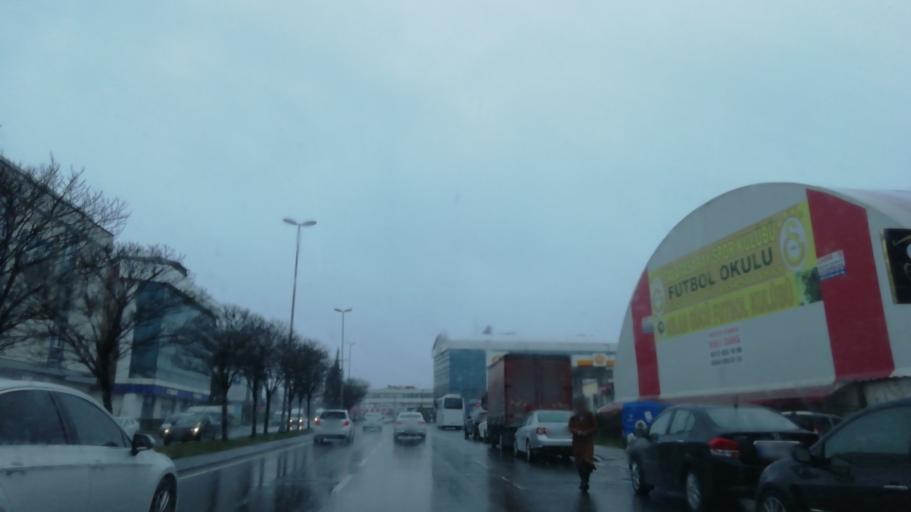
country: TR
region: Istanbul
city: Yakuplu
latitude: 40.9988
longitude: 28.7134
